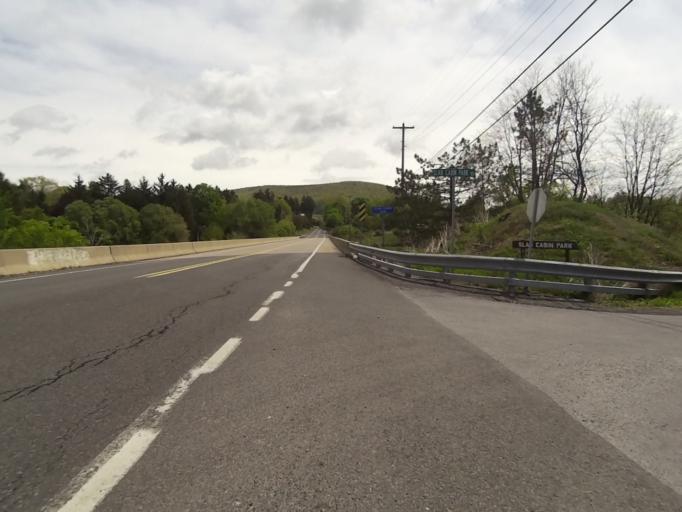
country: US
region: Pennsylvania
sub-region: Centre County
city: Lemont
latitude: 40.8103
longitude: -77.8275
